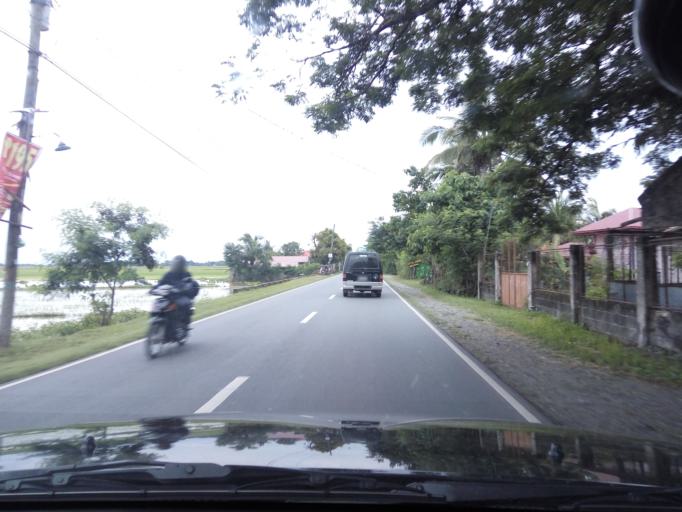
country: PH
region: Central Luzon
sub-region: Province of Nueva Ecija
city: Carmen
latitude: 15.4453
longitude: 120.8337
